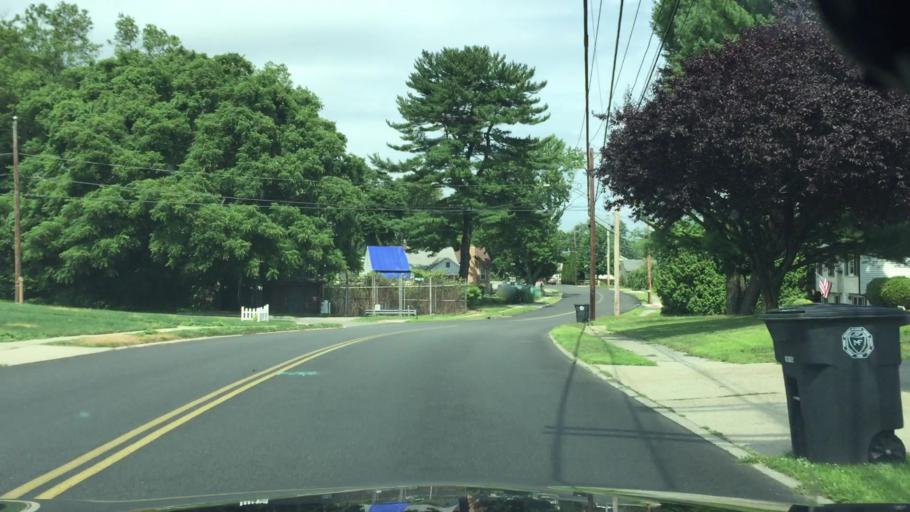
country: US
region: Connecticut
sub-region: New Haven County
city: City of Milford (balance)
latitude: 41.1998
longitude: -73.0911
